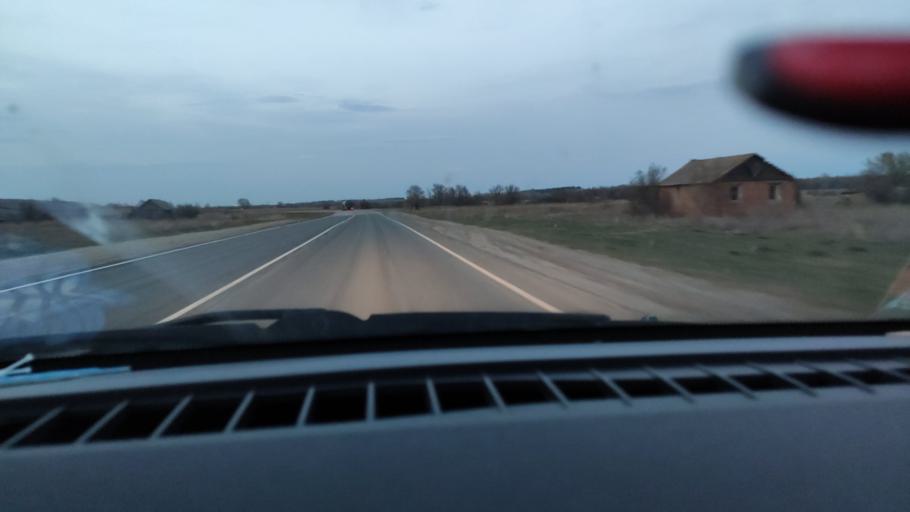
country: RU
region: Saratov
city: Sinodskoye
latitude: 52.0524
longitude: 46.7545
